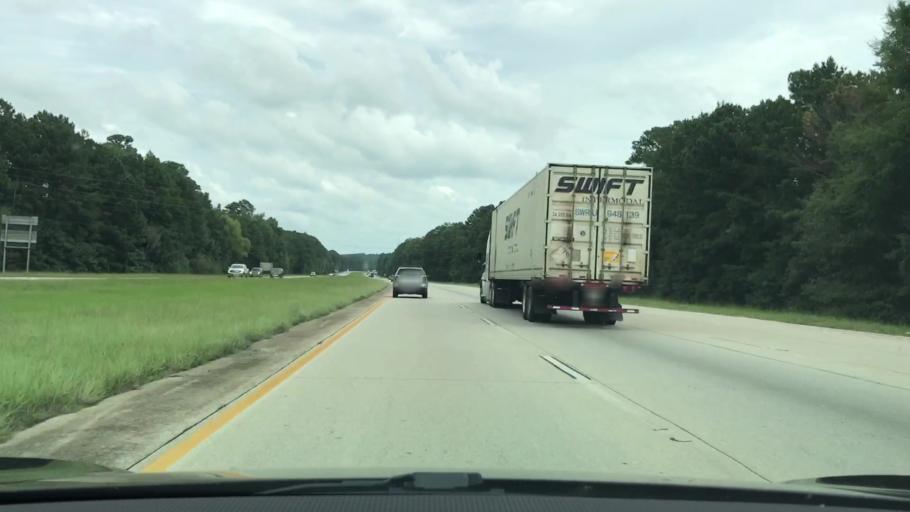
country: US
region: Georgia
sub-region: Troup County
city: La Grange
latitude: 33.0030
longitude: -85.0076
